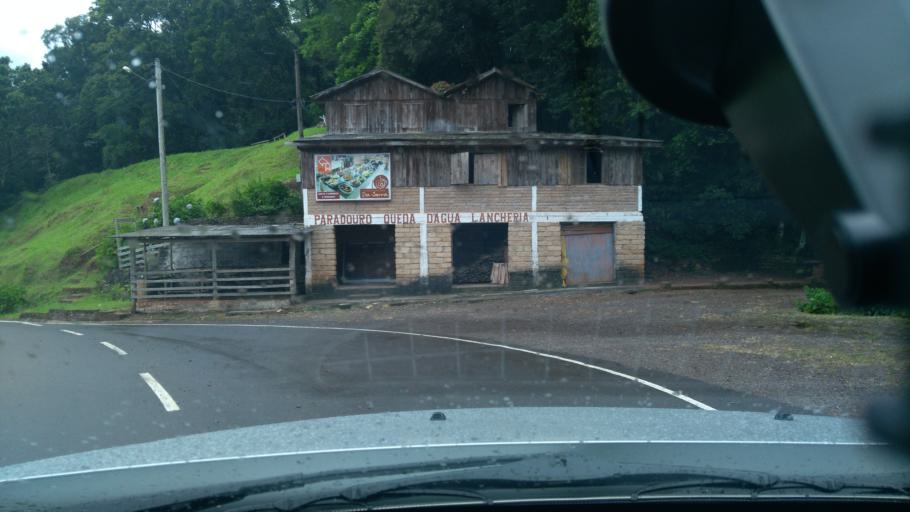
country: BR
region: Rio Grande do Sul
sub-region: Torres
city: Torres
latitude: -29.1862
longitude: -49.9883
